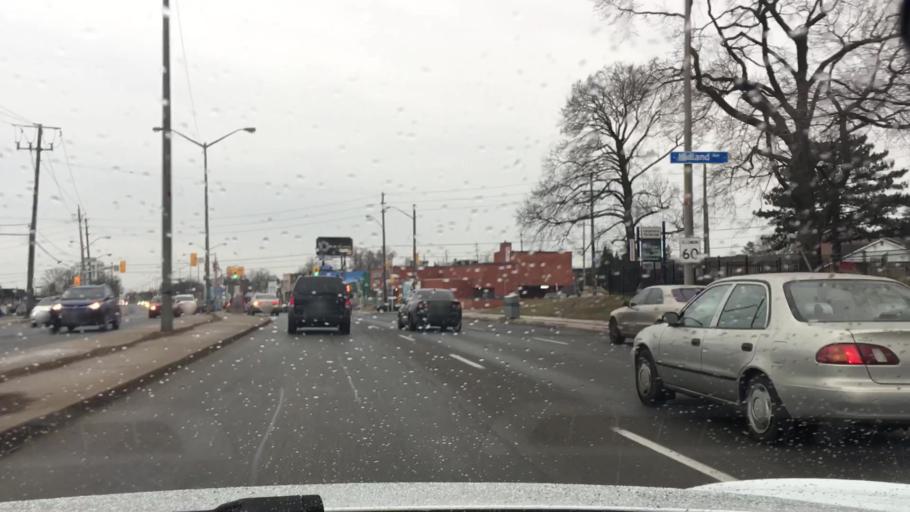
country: CA
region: Ontario
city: Scarborough
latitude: 43.7120
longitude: -79.2475
